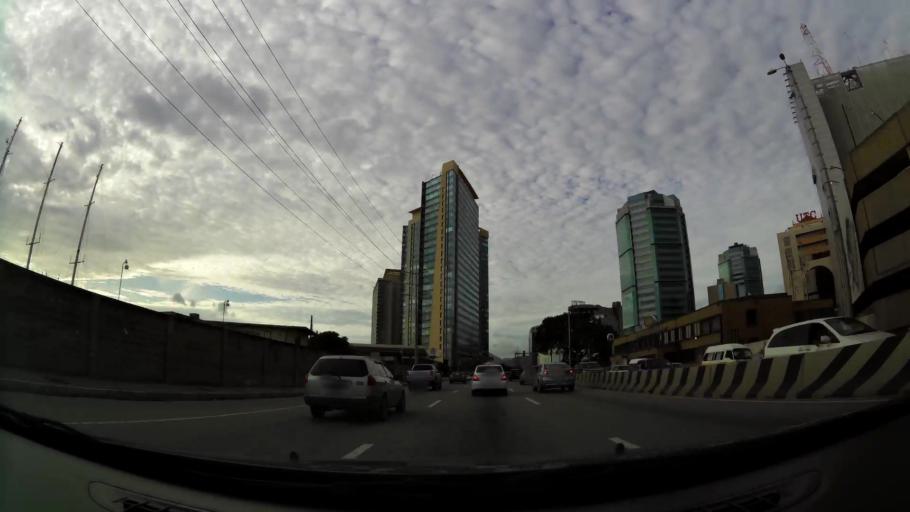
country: TT
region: San Juan/Laventille
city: Laventille
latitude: 10.6485
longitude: -61.5135
